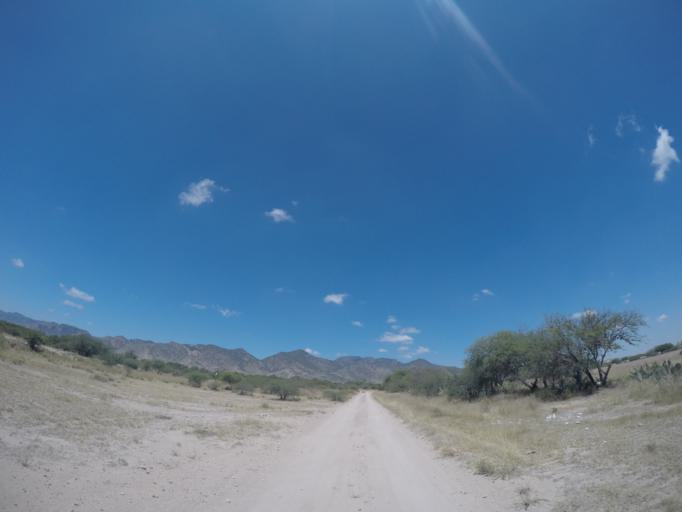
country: MX
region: San Luis Potosi
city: La Pila
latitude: 21.9873
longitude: -100.8971
